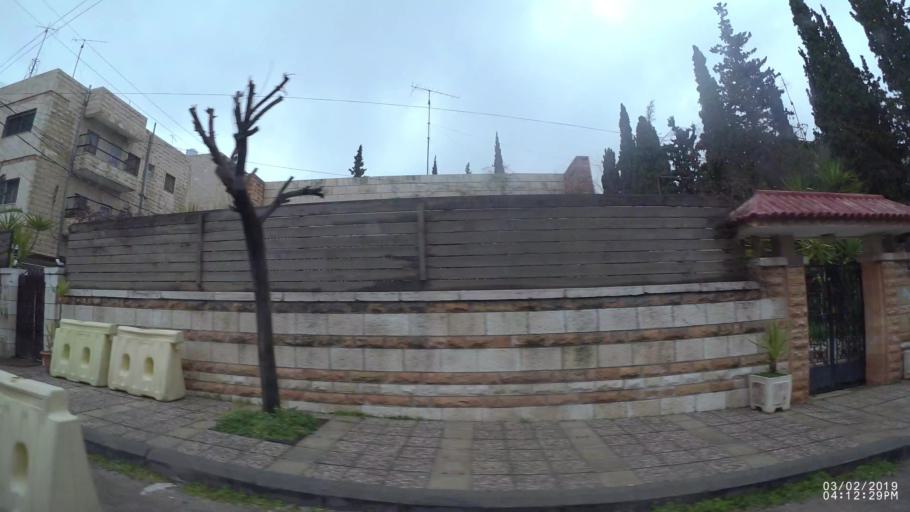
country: JO
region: Amman
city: Amman
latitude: 31.9651
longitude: 35.9176
